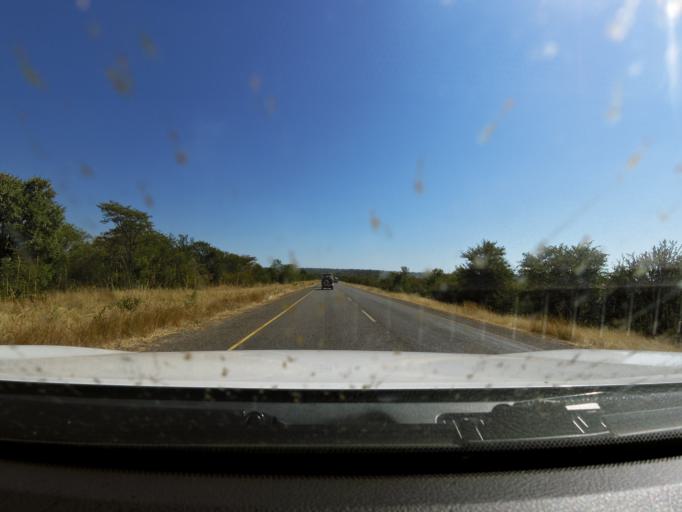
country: ZW
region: Matabeleland North
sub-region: Hwange District
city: Victoria Falls
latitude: -17.9699
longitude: 25.8249
